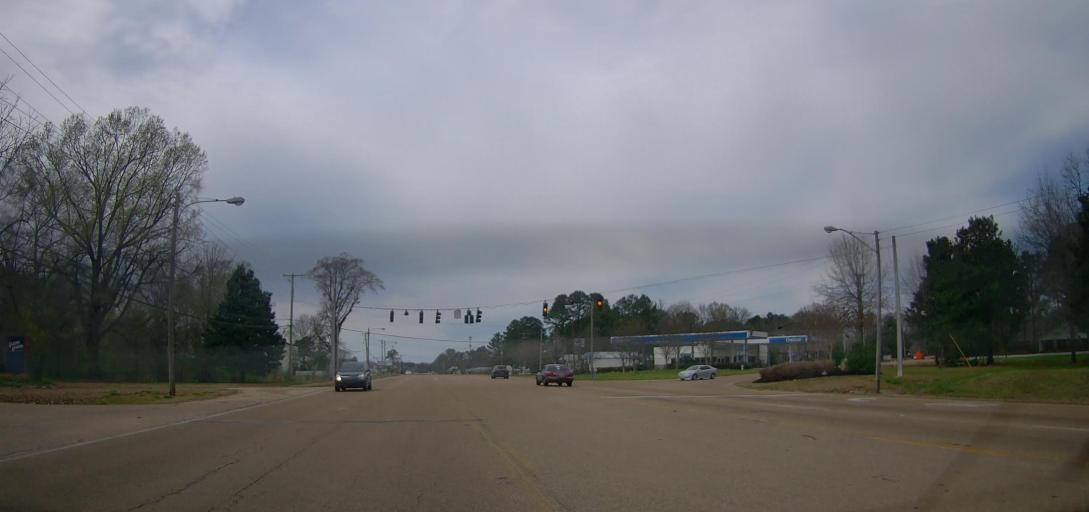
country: US
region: Mississippi
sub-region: Lee County
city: Tupelo
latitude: 34.2847
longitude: -88.7375
